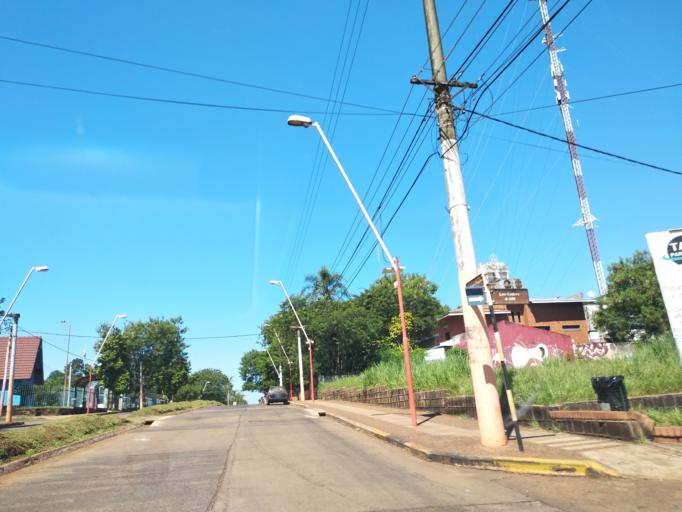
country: AR
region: Misiones
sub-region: Departamento de Iguazu
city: Puerto Iguazu
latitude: -25.6024
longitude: -54.5719
